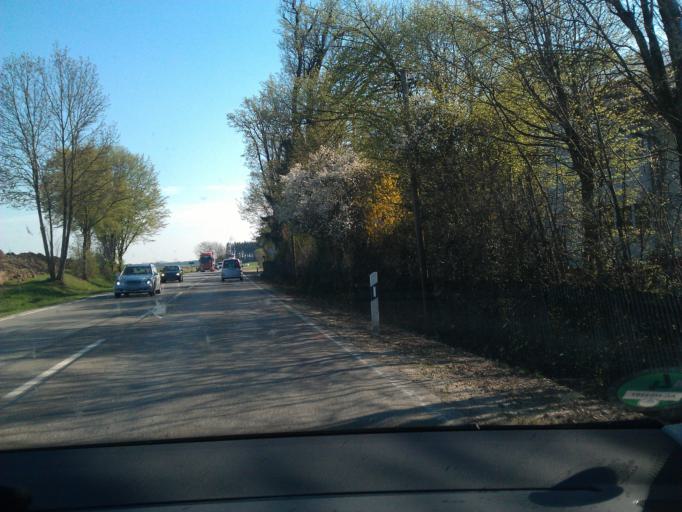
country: DE
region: Bavaria
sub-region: Swabia
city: Obergriesbach
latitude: 48.4090
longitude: 11.0869
